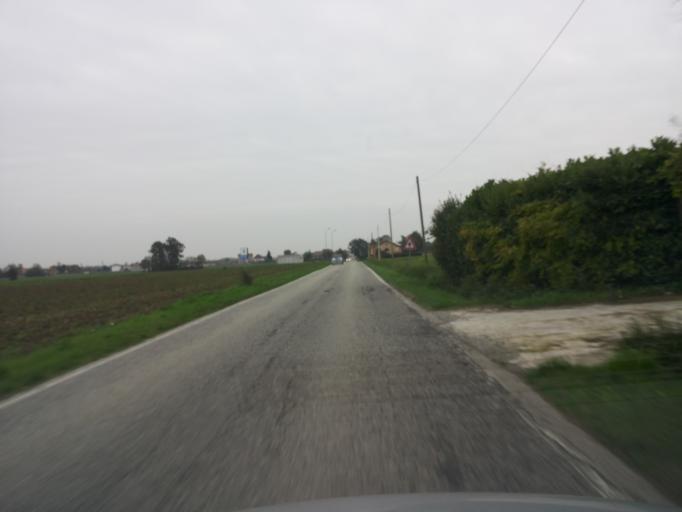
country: IT
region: Piedmont
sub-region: Provincia di Alessandria
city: Terruggia
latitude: 45.1046
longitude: 8.4413
